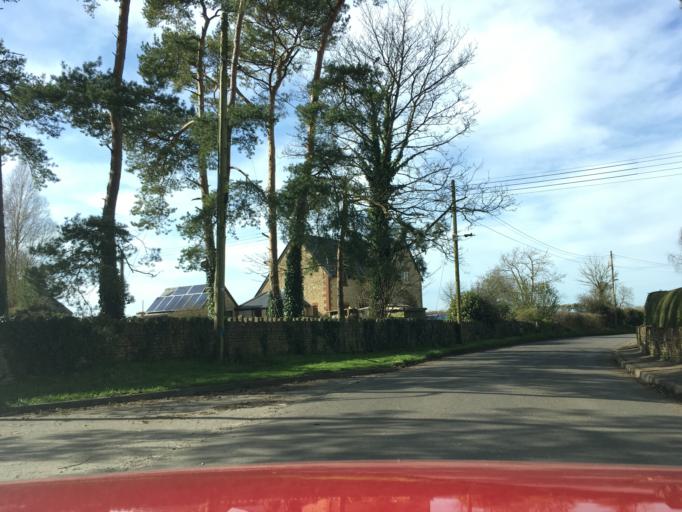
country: GB
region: England
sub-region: Wiltshire
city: Norton
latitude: 51.5182
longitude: -2.1372
